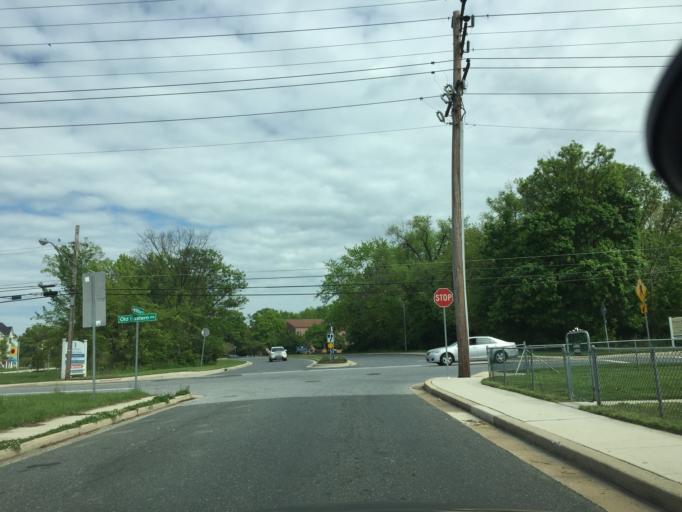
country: US
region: Maryland
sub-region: Baltimore County
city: Middle River
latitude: 39.3235
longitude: -76.4463
